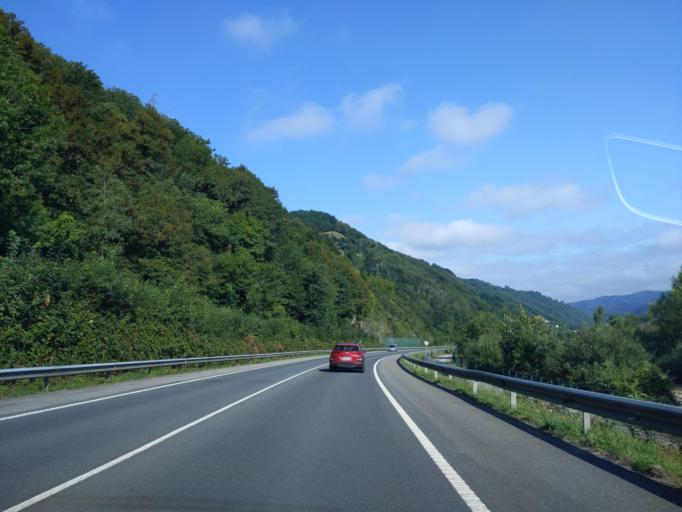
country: ES
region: Asturias
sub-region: Province of Asturias
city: Pola de Laviana
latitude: 43.2365
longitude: -5.5616
